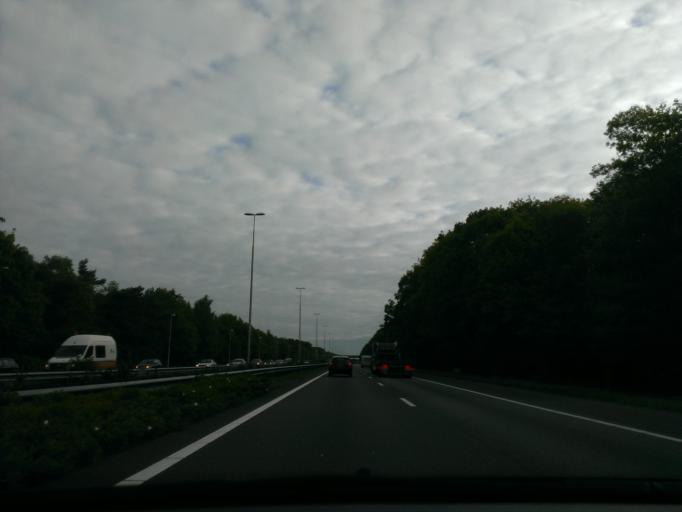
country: NL
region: Gelderland
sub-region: Gemeente Heerde
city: Heerde
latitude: 52.4015
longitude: 6.0150
